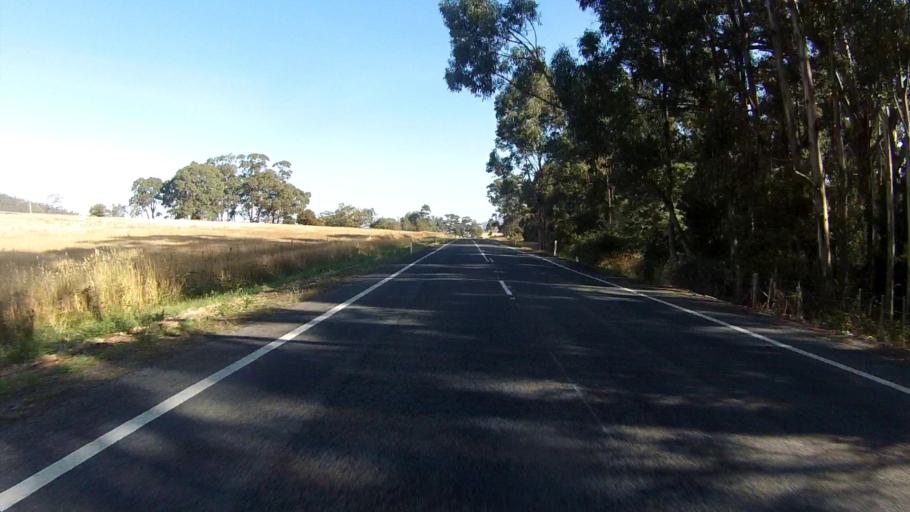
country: AU
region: Tasmania
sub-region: Sorell
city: Sorell
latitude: -42.6969
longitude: 147.5257
